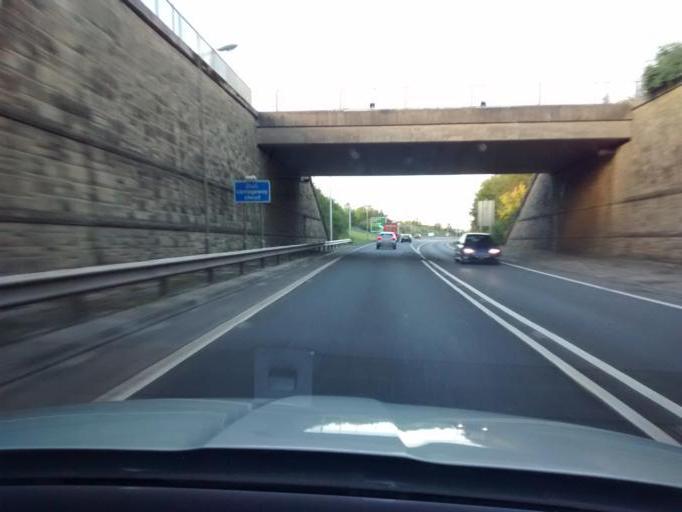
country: GB
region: Scotland
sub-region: Renfrewshire
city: Kilbarchan
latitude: 55.8305
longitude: -4.5356
